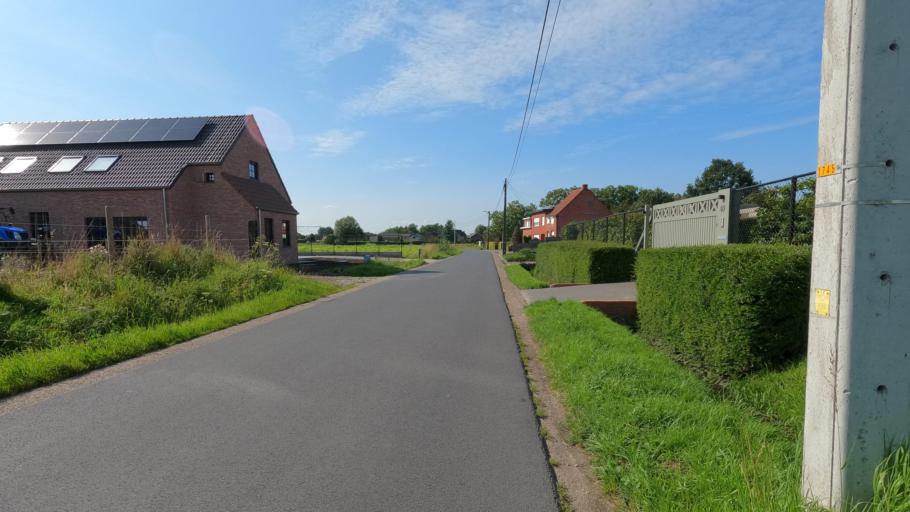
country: BE
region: Flanders
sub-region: Provincie Antwerpen
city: Berlaar
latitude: 51.0977
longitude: 4.6679
